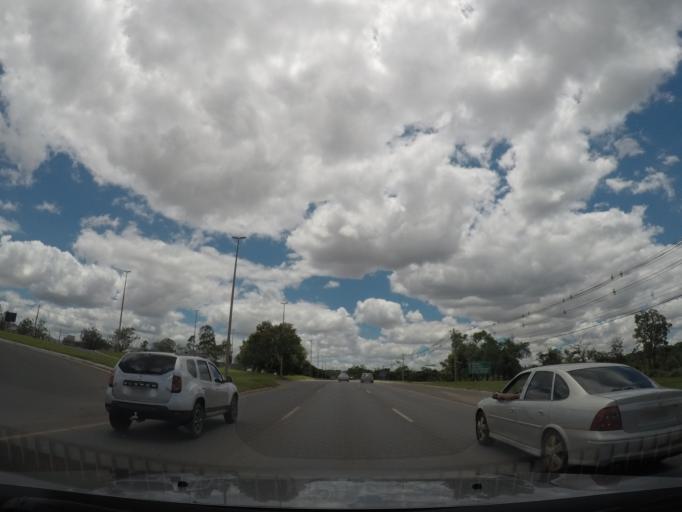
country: BR
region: Federal District
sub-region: Brasilia
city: Brasilia
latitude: -15.7335
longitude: -47.9130
